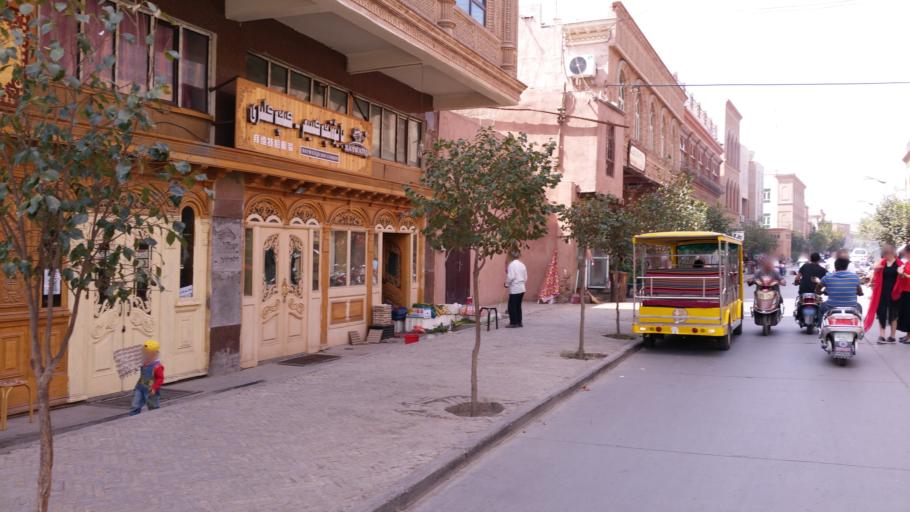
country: CN
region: Xinjiang Uygur Zizhiqu
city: Kashi
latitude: 39.4705
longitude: 75.9826
